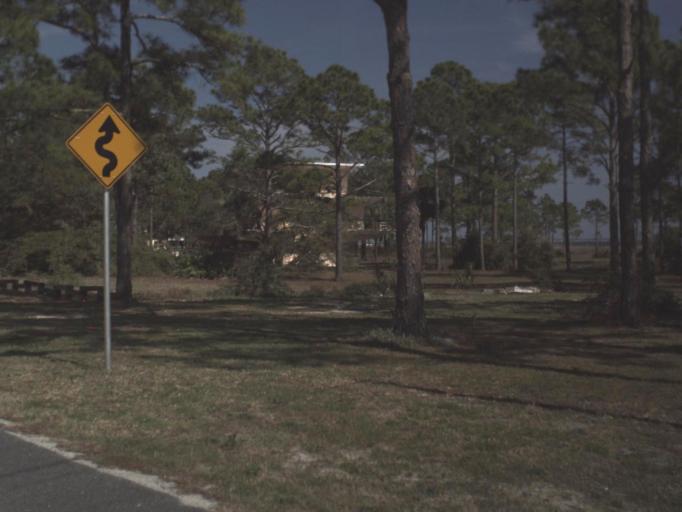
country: US
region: Florida
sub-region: Franklin County
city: Carrabelle
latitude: 29.8315
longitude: -84.6890
